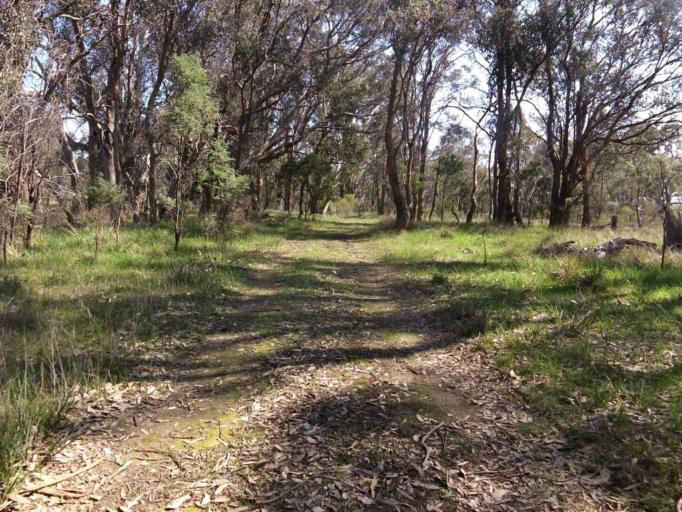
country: AU
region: Victoria
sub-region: Murrindindi
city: Alexandra
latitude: -36.9783
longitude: 145.7092
